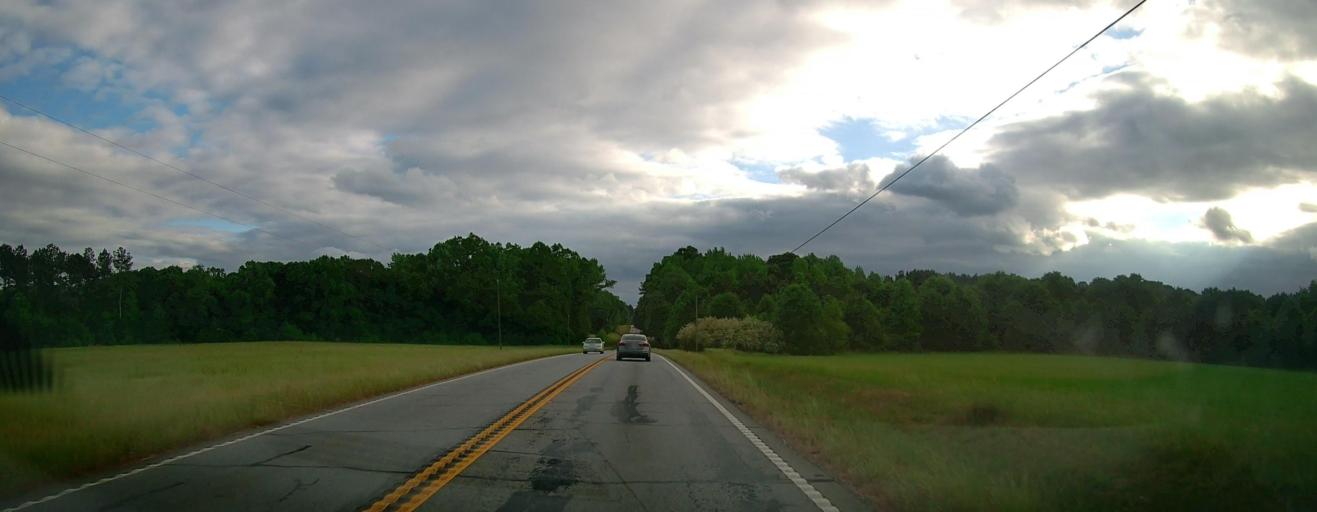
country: US
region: Georgia
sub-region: Oconee County
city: Watkinsville
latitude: 33.8384
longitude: -83.4286
